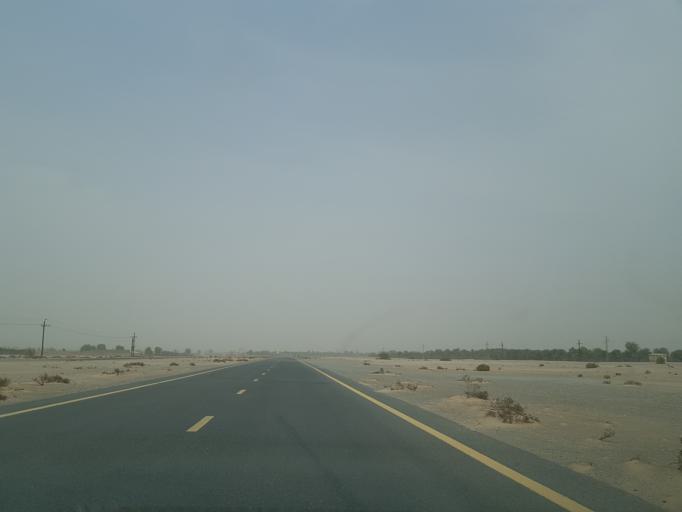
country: AE
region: Dubai
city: Dubai
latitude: 24.9373
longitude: 55.4750
